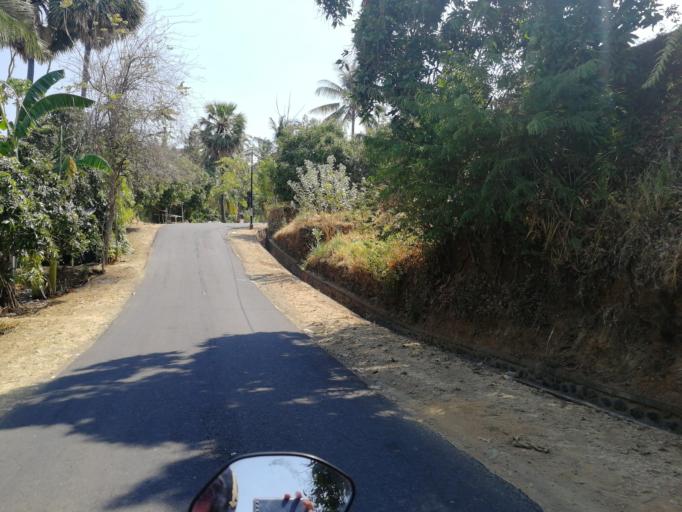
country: ID
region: Bali
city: Banjar Trunyan
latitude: -8.1325
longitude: 115.3248
